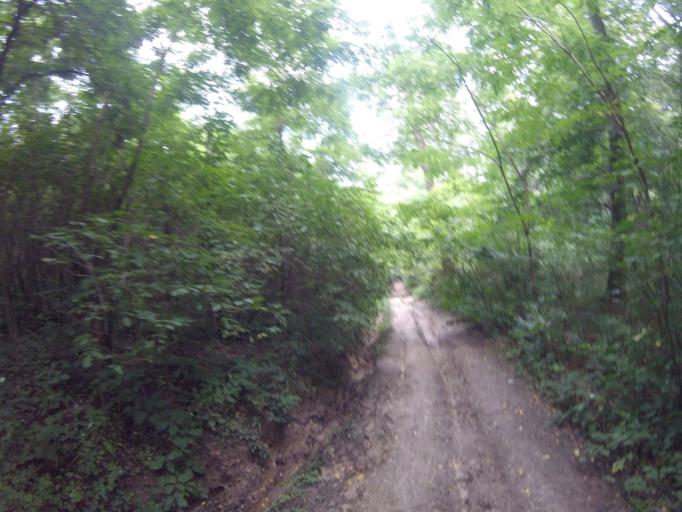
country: HU
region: Zala
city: Nagykanizsa
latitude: 46.5598
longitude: 17.0344
